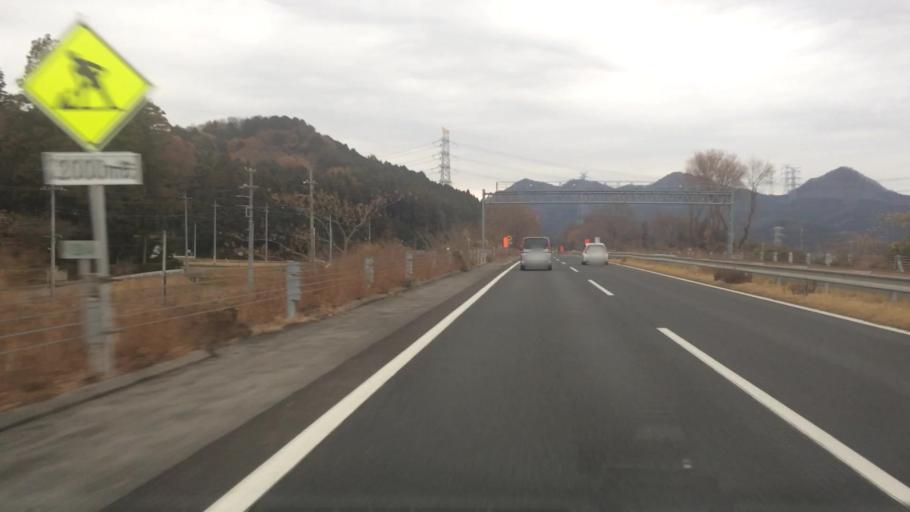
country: JP
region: Tochigi
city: Utsunomiya-shi
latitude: 36.6555
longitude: 139.8359
